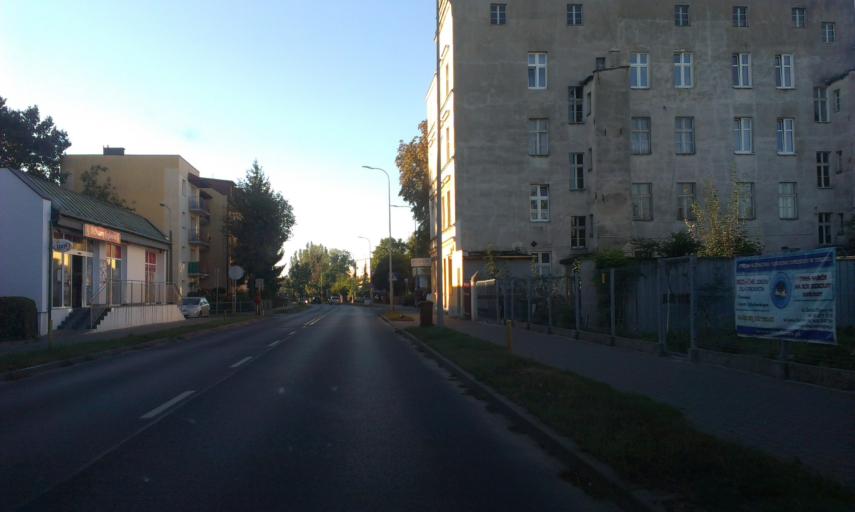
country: PL
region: Kujawsko-Pomorskie
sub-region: Torun
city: Torun
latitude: 53.0217
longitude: 18.6019
